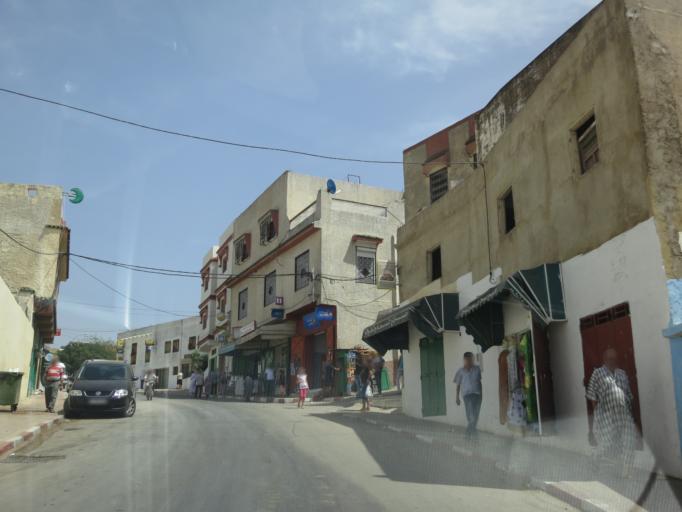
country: MA
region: Meknes-Tafilalet
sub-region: Meknes
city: Meknes
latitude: 34.0569
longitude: -5.5217
